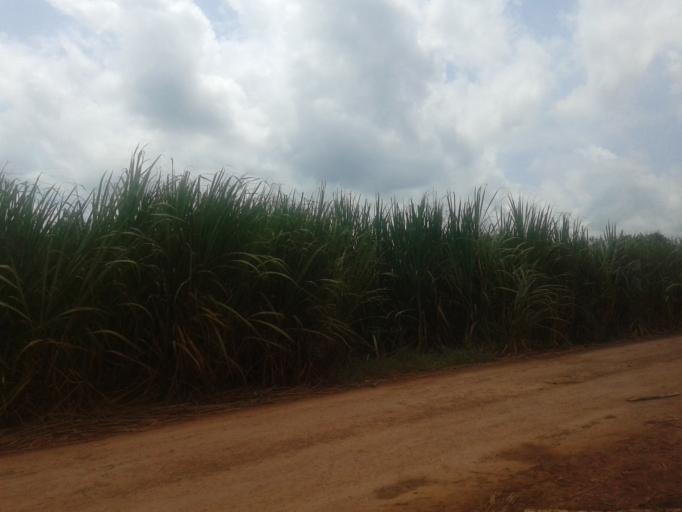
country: CM
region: Centre
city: Mbandjok
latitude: 4.4468
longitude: 11.9588
